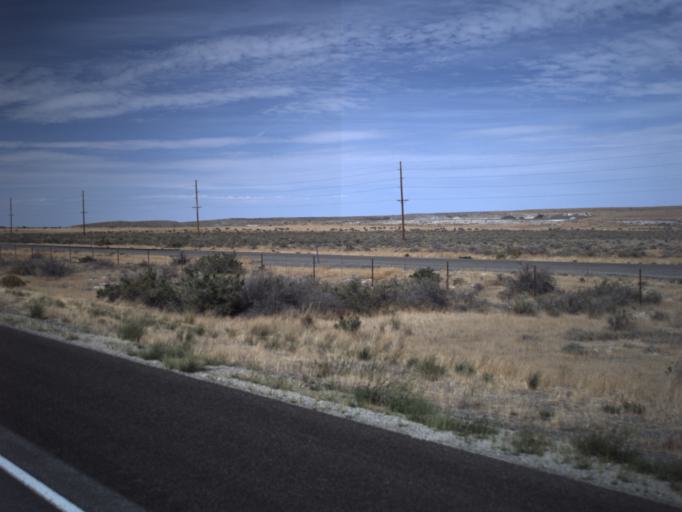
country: US
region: Utah
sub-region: Tooele County
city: Grantsville
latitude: 40.7289
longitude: -113.1267
